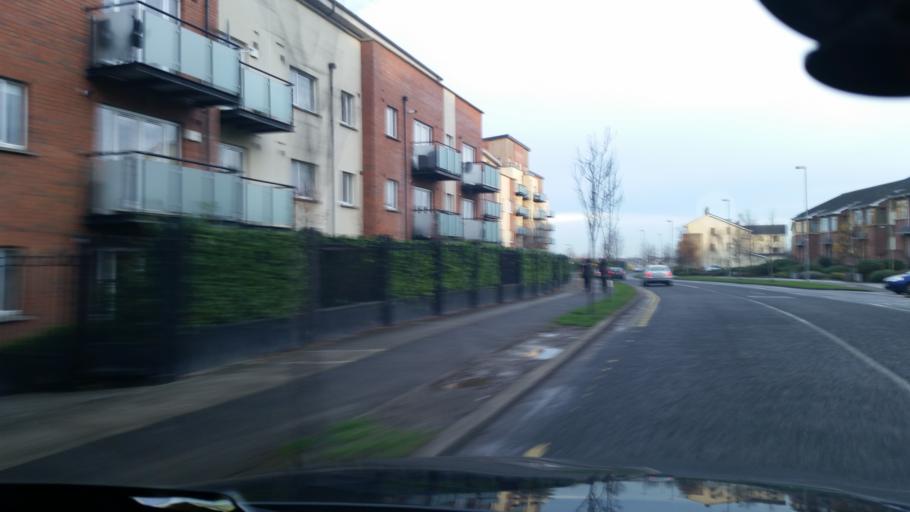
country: IE
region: Leinster
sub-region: Dublin City
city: Finglas
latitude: 53.4062
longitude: -6.2875
